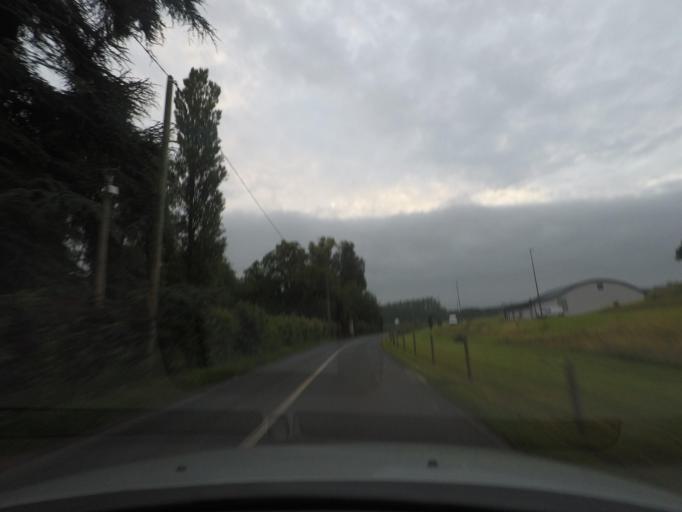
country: FR
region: Haute-Normandie
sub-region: Departement de la Seine-Maritime
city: Fontaine-le-Bourg
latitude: 49.5603
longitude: 1.1503
